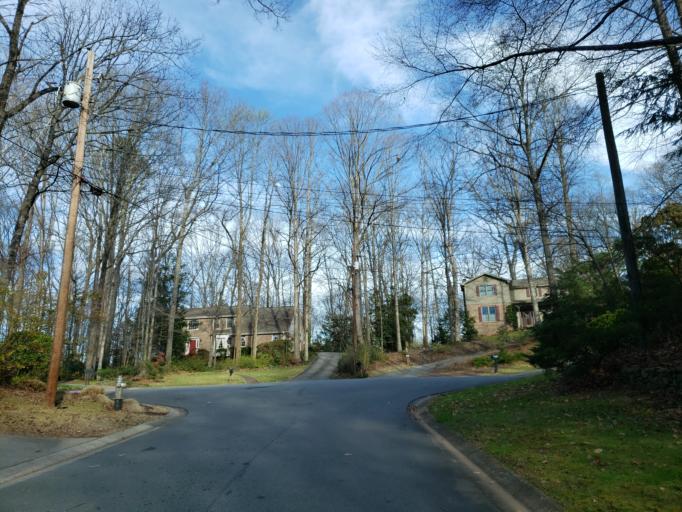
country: US
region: Georgia
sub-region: Cobb County
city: Marietta
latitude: 33.9487
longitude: -84.4798
